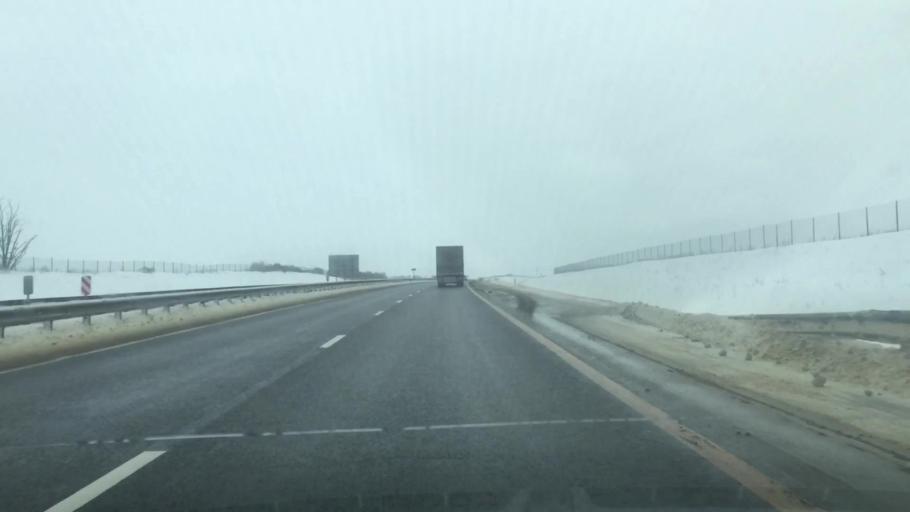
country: RU
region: Tula
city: Yefremov
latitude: 53.1542
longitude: 38.2503
